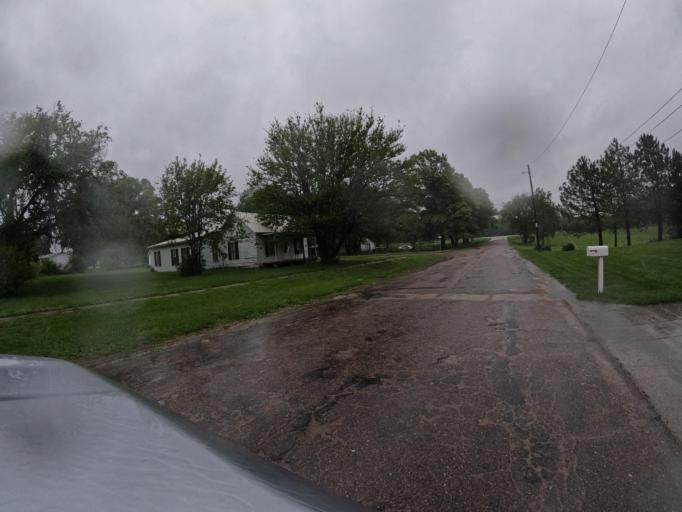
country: US
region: Nebraska
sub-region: Gage County
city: Wymore
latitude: 40.1168
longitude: -96.6732
